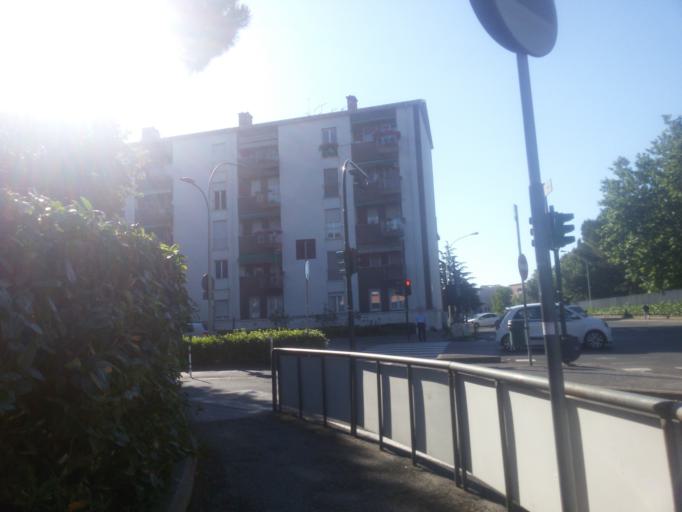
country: IT
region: Liguria
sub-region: Provincia di La Spezia
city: La Spezia
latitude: 44.1176
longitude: 9.8423
